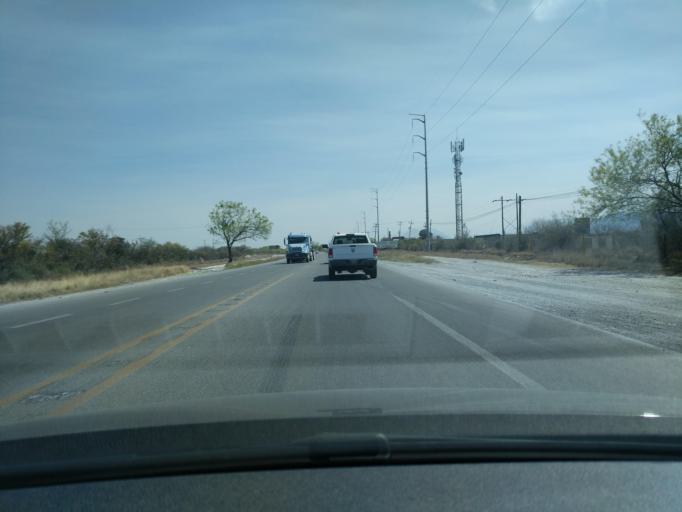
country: MX
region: Nuevo Leon
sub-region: El Carmen
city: Buena Vista
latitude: 25.8969
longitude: -100.3522
